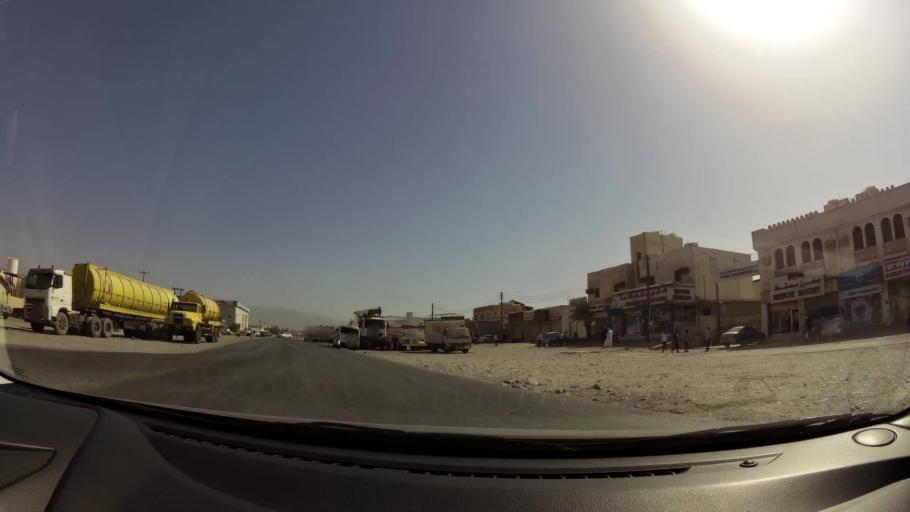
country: OM
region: Muhafazat Masqat
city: Bawshar
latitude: 23.5766
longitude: 58.3535
